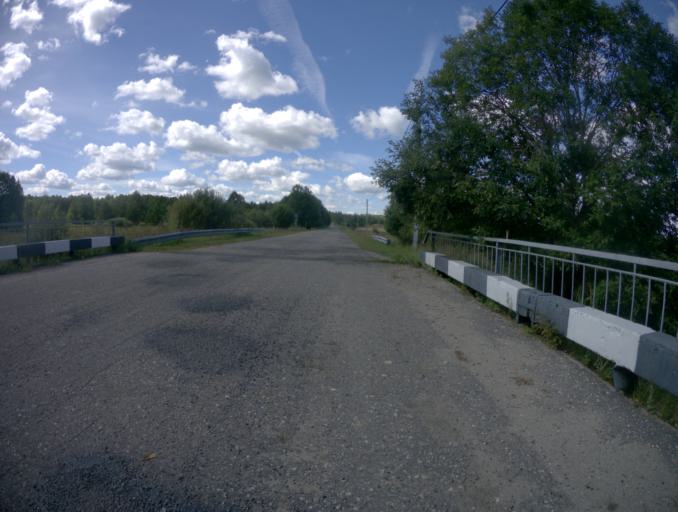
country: RU
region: Vladimir
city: Krasnaya Gorbatka
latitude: 55.9820
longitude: 41.8779
